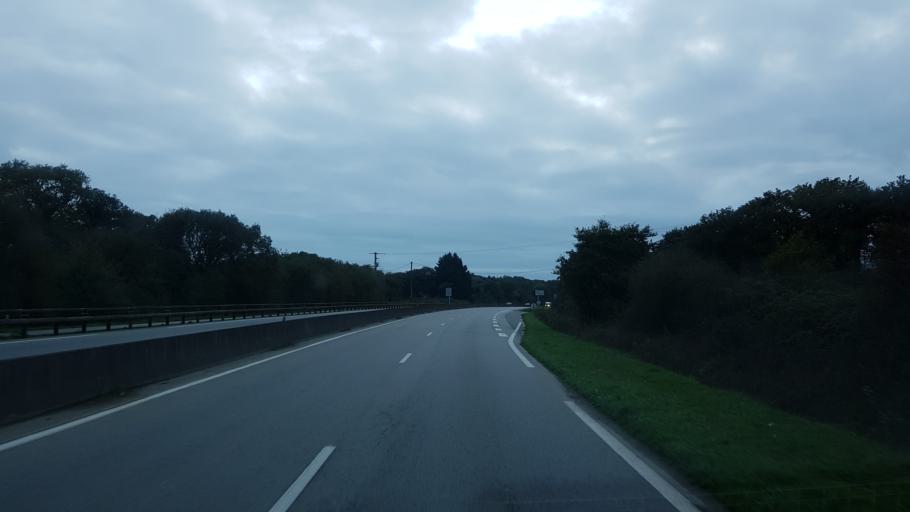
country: FR
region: Brittany
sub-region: Departement du Morbihan
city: Sarzeau
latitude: 47.5454
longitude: -2.7215
